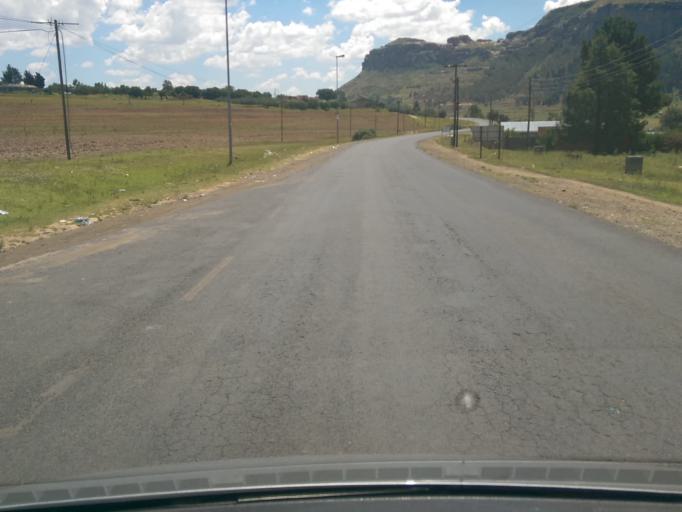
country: LS
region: Maseru
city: Nako
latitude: -29.4397
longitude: 27.7039
